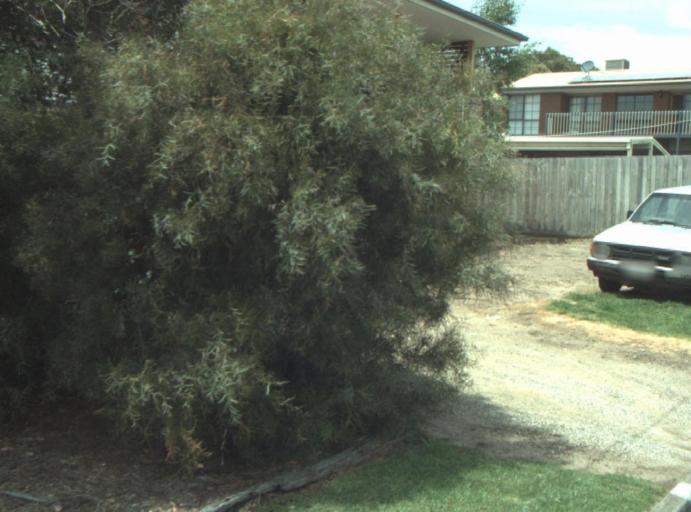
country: AU
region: Victoria
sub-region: Greater Geelong
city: Clifton Springs
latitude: -38.1606
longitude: 144.5599
